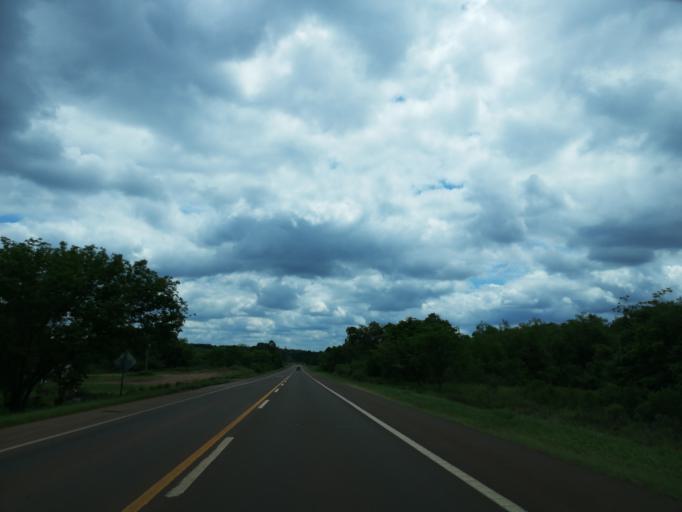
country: AR
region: Misiones
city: Arroyo del Medio
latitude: -27.6420
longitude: -55.3847
